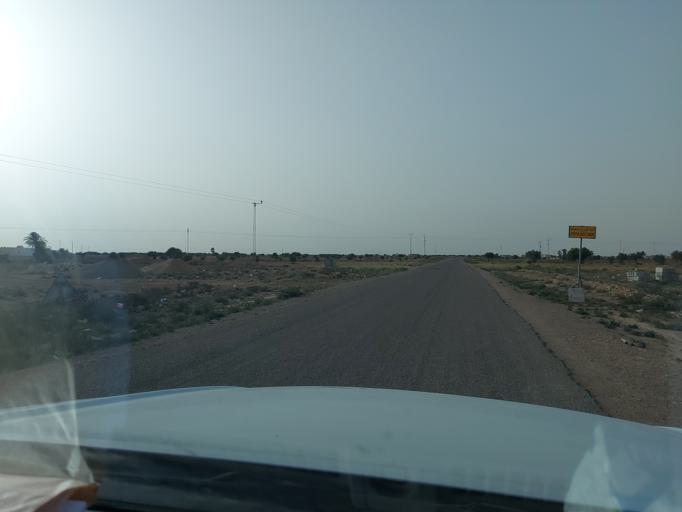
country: TN
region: Madanin
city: Medenine
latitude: 33.3532
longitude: 10.5871
